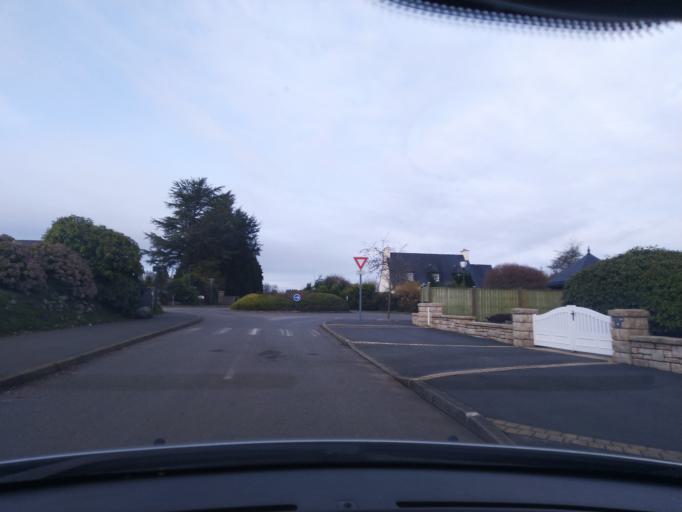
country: FR
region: Brittany
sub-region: Departement du Finistere
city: Guerlesquin
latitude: 48.5176
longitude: -3.5962
